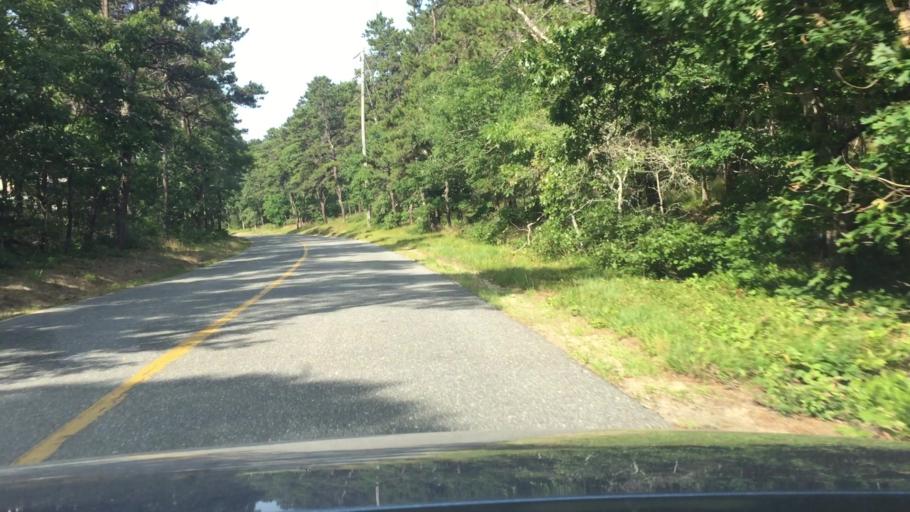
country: US
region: Massachusetts
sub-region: Barnstable County
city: Truro
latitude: 42.0327
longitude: -70.0693
